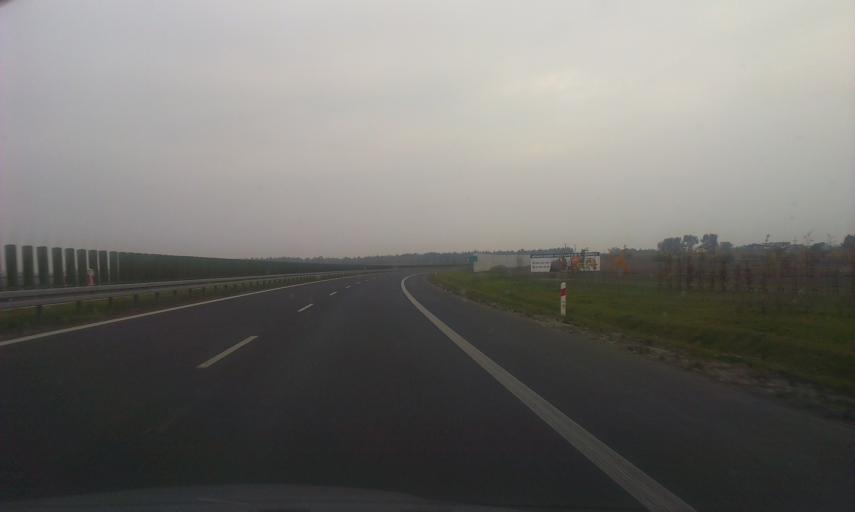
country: PL
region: Greater Poland Voivodeship
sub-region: Powiat poznanski
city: Rokietnica
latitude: 52.4670
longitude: 16.7325
